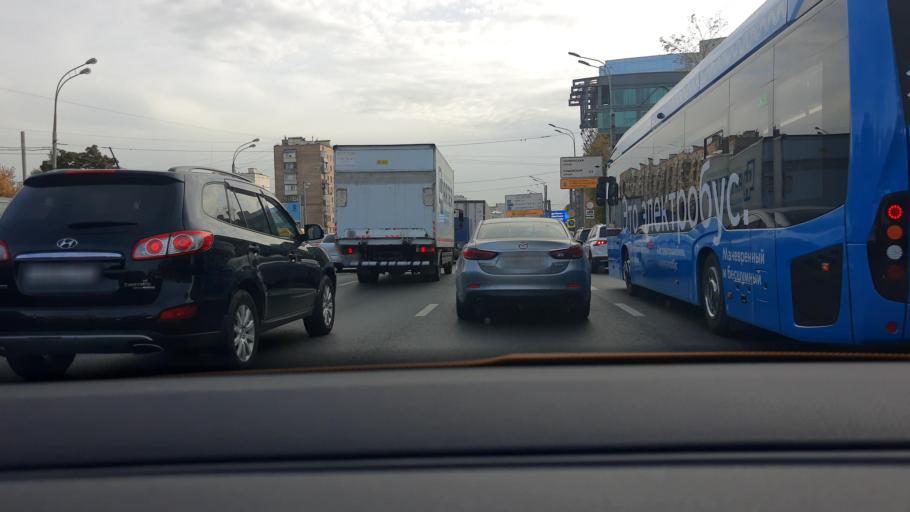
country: RU
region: Moscow
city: Mar'ina Roshcha
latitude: 55.7928
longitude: 37.5935
